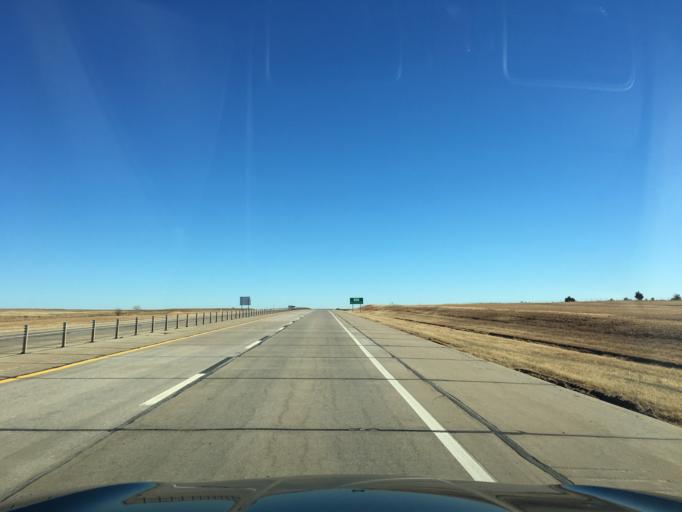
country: US
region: Oklahoma
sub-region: Noble County
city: Perry
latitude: 36.3998
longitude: -97.3091
